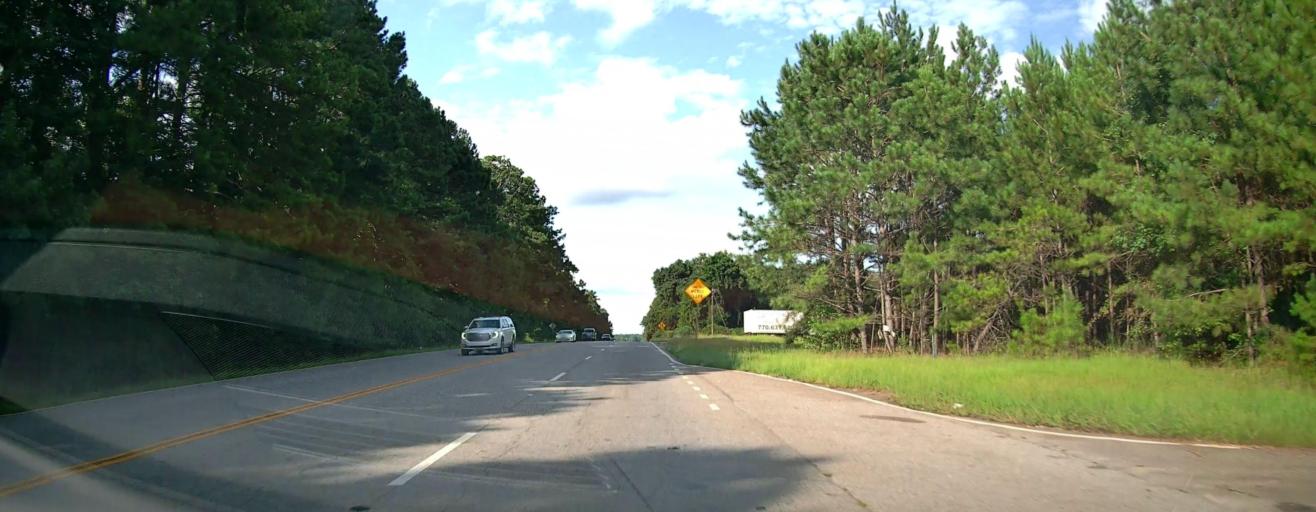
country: US
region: Georgia
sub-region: Coweta County
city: Senoia
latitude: 33.3103
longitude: -84.5298
